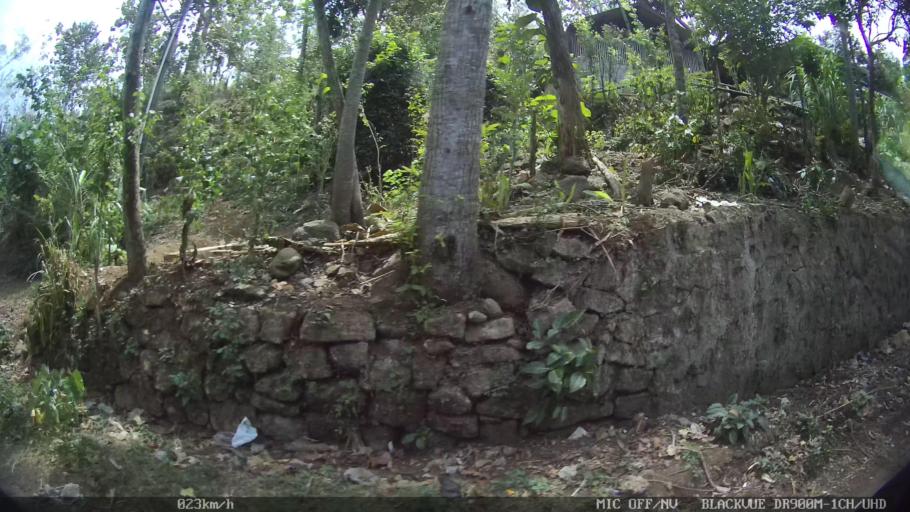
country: ID
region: Central Java
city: Candi Prambanan
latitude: -7.8187
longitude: 110.5206
